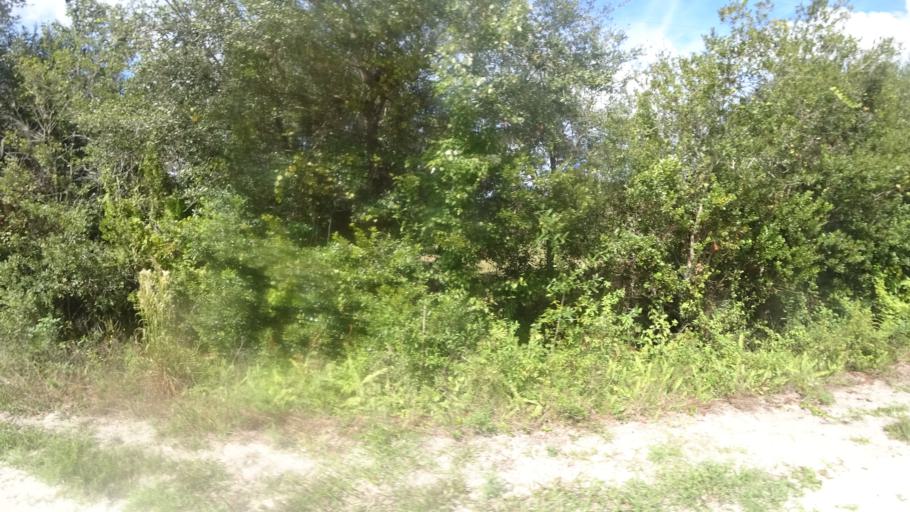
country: US
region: Florida
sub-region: Hillsborough County
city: Sun City Center
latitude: 27.6346
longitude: -82.3619
